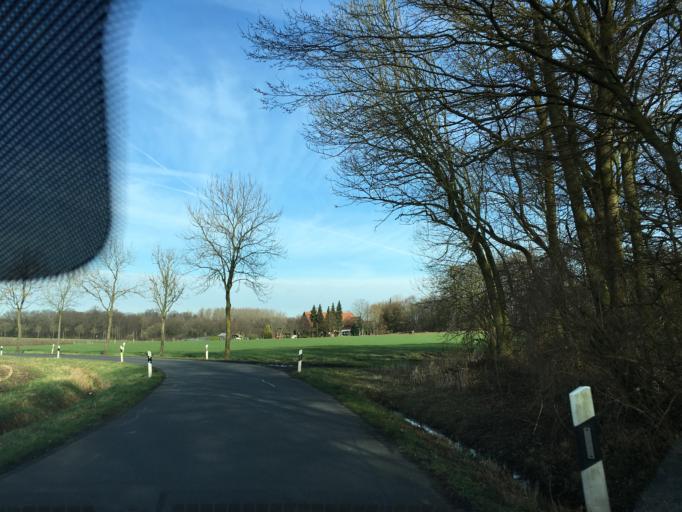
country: DE
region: North Rhine-Westphalia
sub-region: Regierungsbezirk Munster
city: Muenster
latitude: 52.0082
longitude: 7.5758
